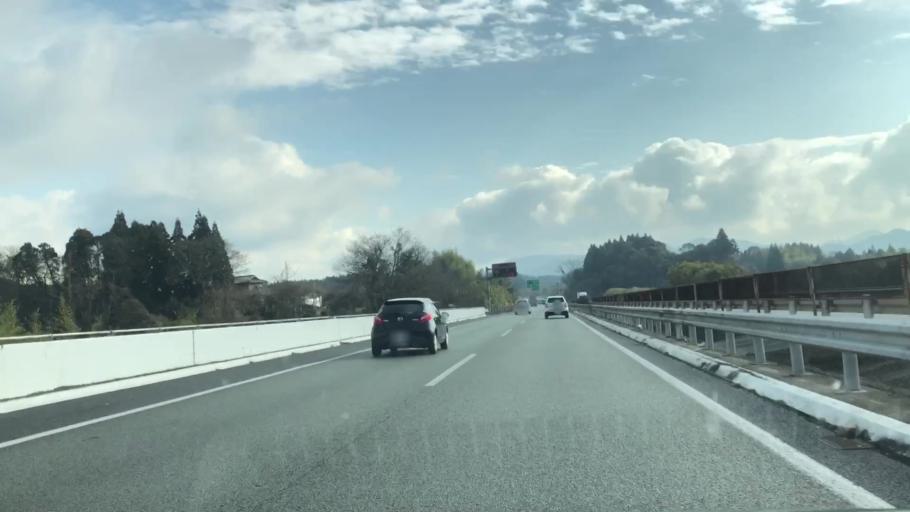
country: JP
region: Kumamoto
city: Tamana
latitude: 32.9917
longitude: 130.6022
